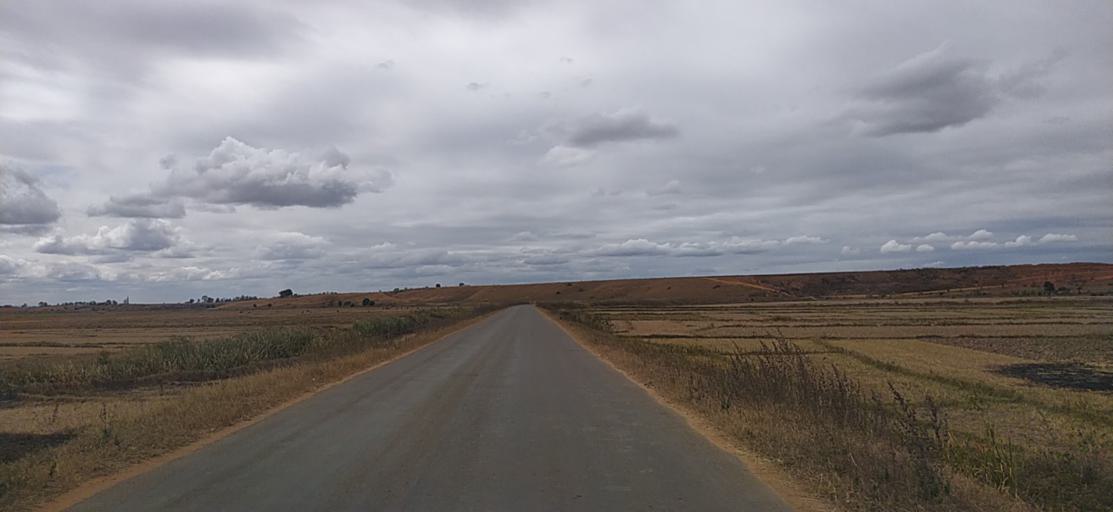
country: MG
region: Alaotra Mangoro
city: Ambatondrazaka
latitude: -17.9175
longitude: 48.2583
